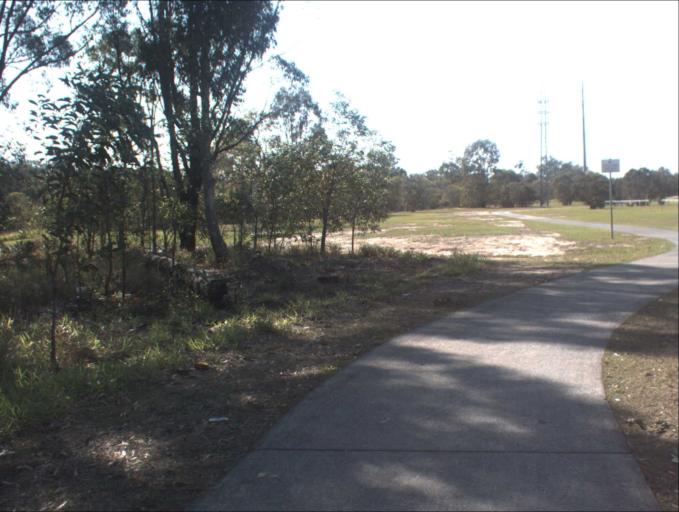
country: AU
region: Queensland
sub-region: Logan
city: Logan City
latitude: -27.6674
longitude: 153.1036
